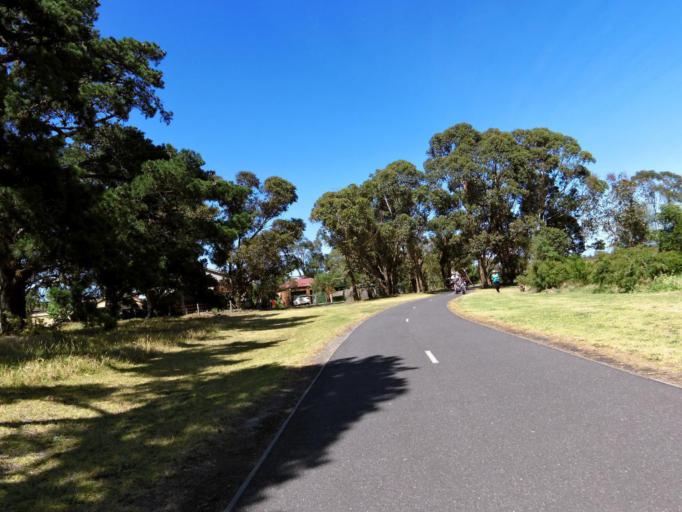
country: AU
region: Victoria
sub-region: Frankston
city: Seaford
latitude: -38.0946
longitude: 145.1438
